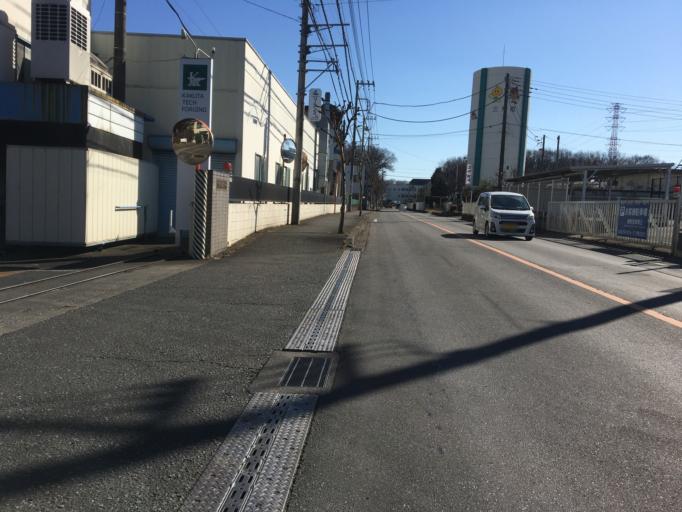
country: JP
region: Saitama
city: Oi
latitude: 35.8314
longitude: 139.5237
